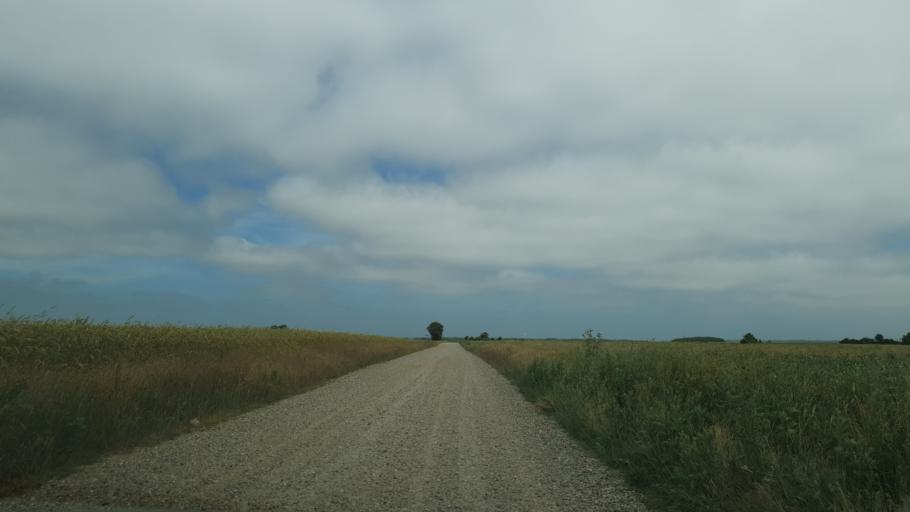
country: DK
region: Central Jutland
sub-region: Ringkobing-Skjern Kommune
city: Skjern
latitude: 55.9354
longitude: 8.4067
